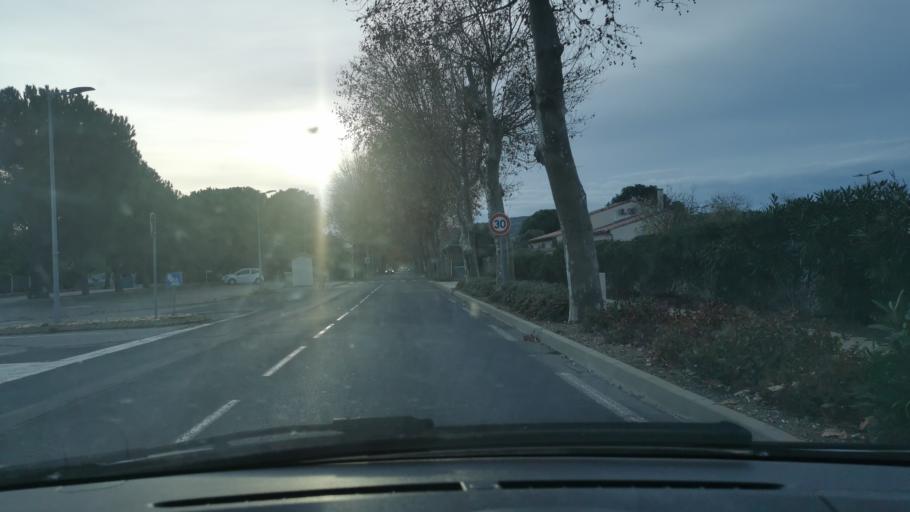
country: FR
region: Languedoc-Roussillon
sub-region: Departement de l'Herault
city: Mireval
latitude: 43.5062
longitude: 3.7963
